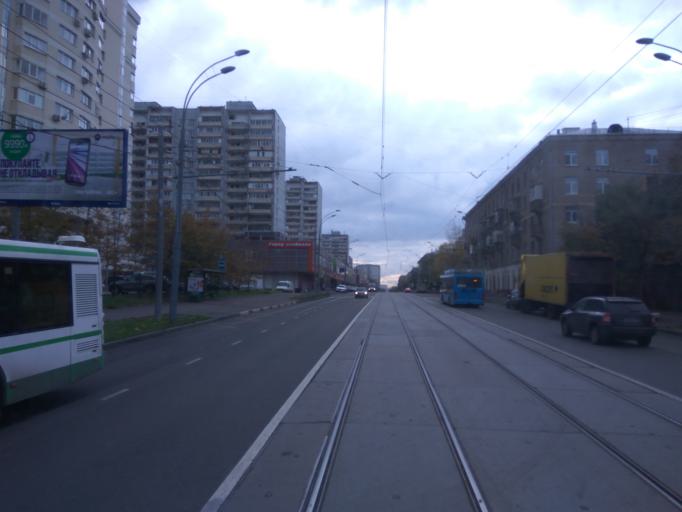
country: RU
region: Moskovskaya
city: Izmaylovo
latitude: 55.7936
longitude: 37.8177
